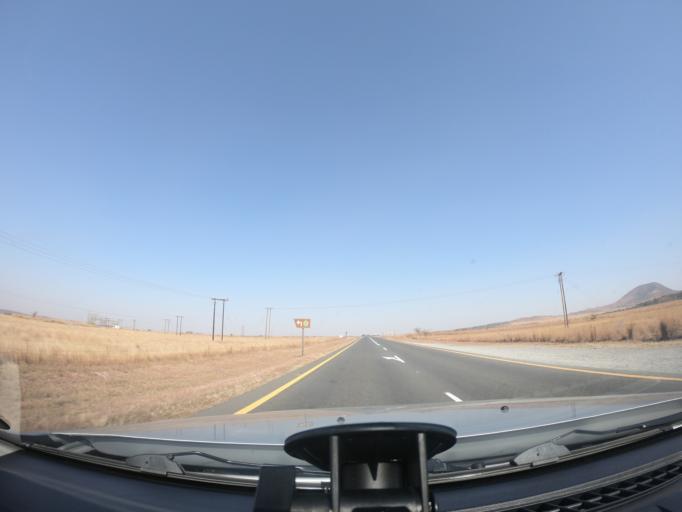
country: ZA
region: KwaZulu-Natal
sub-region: uThukela District Municipality
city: Ekuvukeni
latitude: -28.3775
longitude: 29.9456
